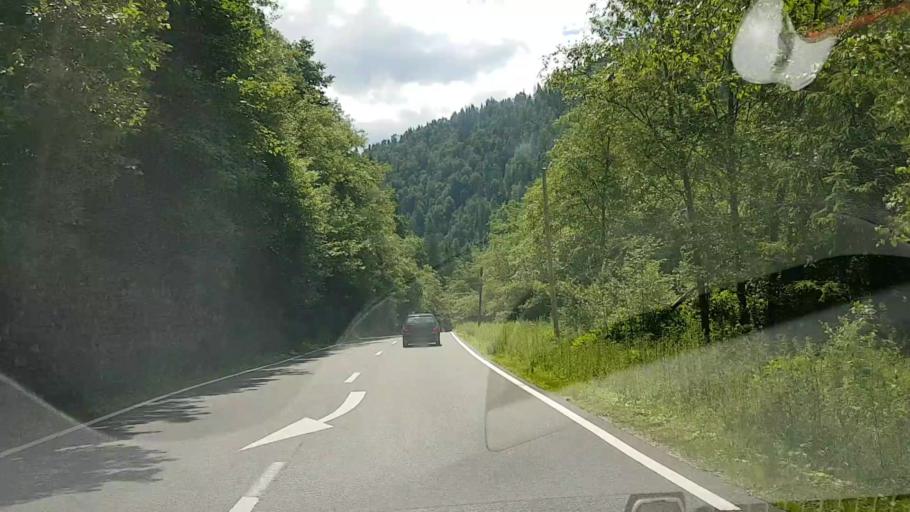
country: RO
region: Suceava
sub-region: Comuna Brosteni
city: Brosteni
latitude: 47.2786
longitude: 25.6499
